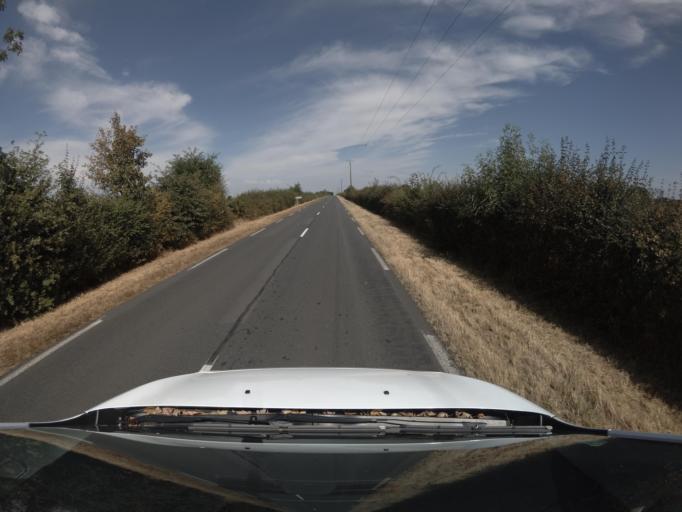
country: FR
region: Poitou-Charentes
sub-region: Departement des Deux-Sevres
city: Argenton-les-Vallees
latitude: 46.9791
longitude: -0.5135
